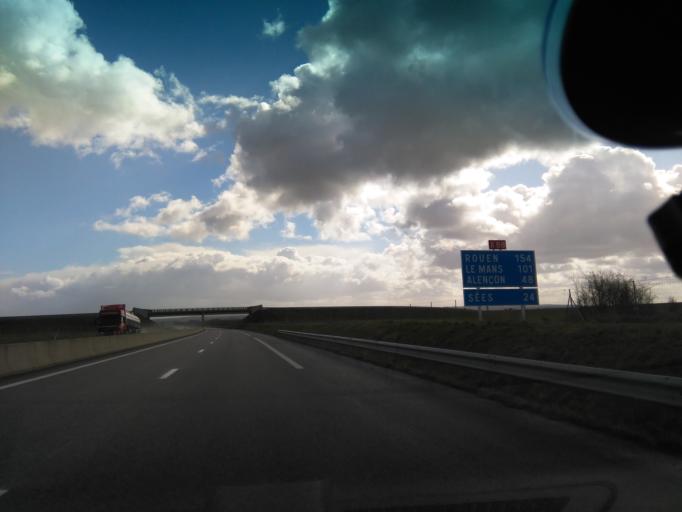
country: FR
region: Lower Normandy
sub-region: Departement de l'Orne
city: Argentan
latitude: 48.7118
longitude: -0.0539
